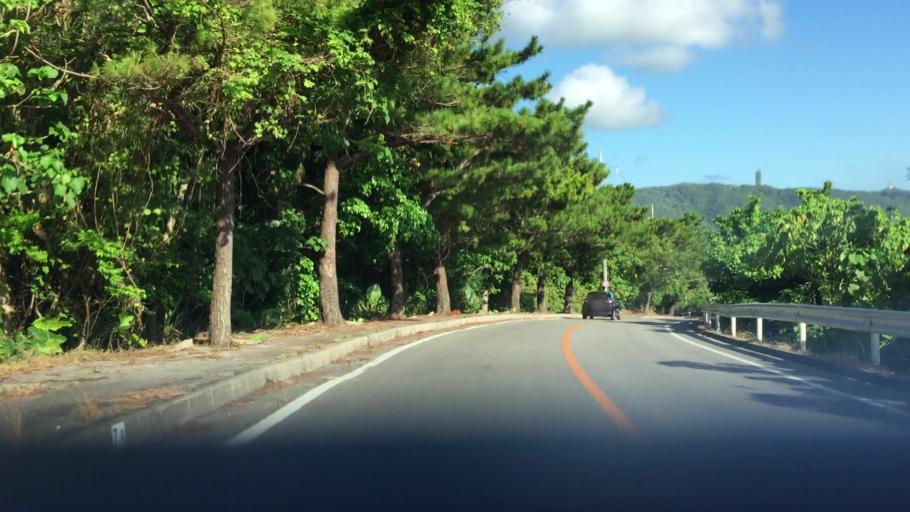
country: JP
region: Okinawa
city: Ishigaki
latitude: 24.4050
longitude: 124.1464
